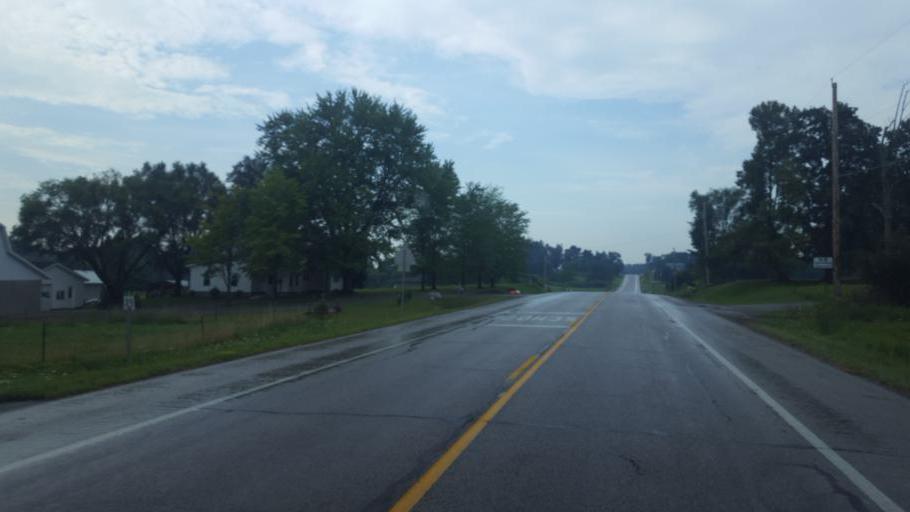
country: US
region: Ohio
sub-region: Ashtabula County
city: Orwell
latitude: 41.4735
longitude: -80.9513
